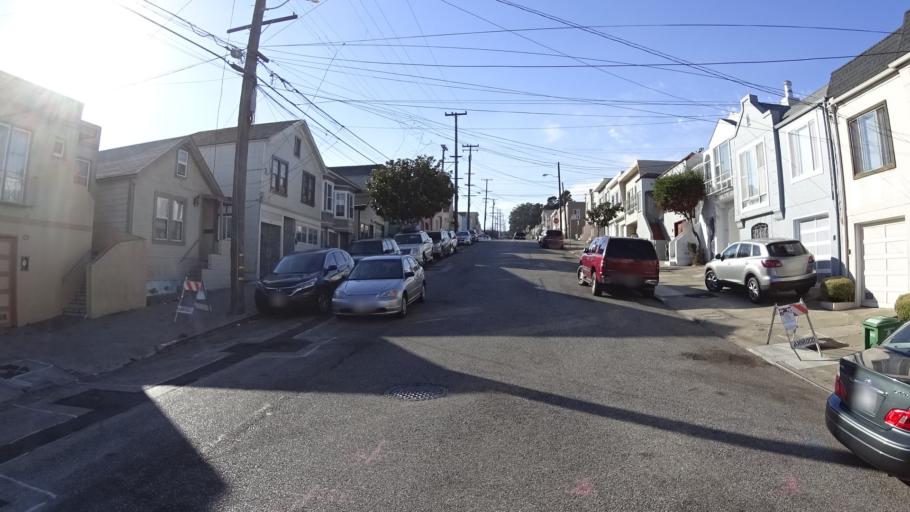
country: US
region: California
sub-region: San Mateo County
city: Brisbane
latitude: 37.7136
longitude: -122.4083
